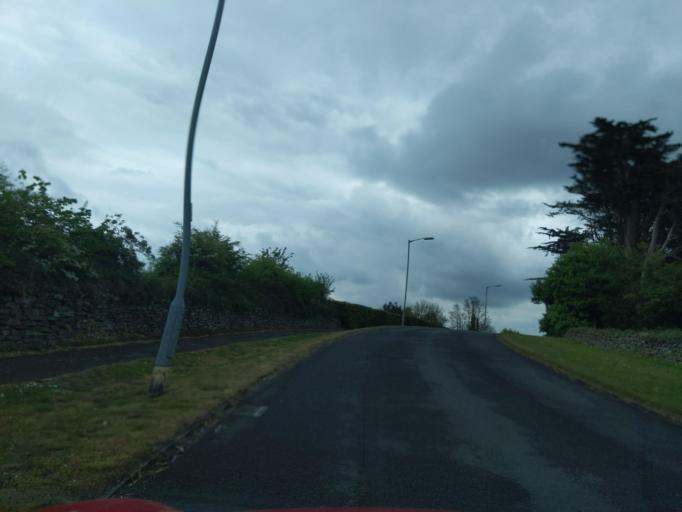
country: GB
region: England
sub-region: Cornwall
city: Saltash
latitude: 50.4179
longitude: -4.2171
